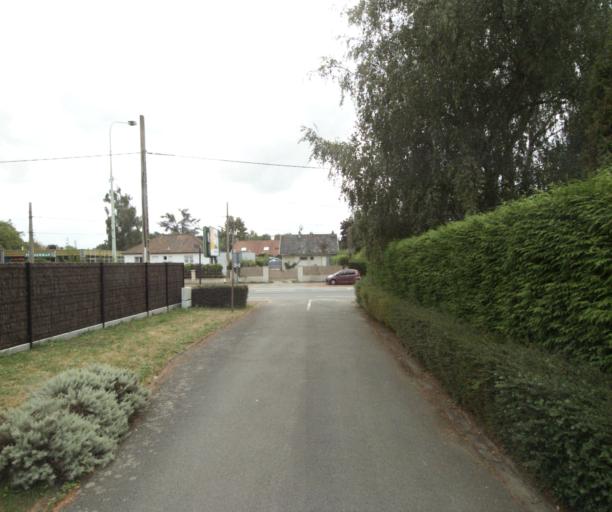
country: FR
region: Nord-Pas-de-Calais
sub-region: Departement du Nord
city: Villeneuve-d'Ascq
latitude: 50.6169
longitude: 3.1500
